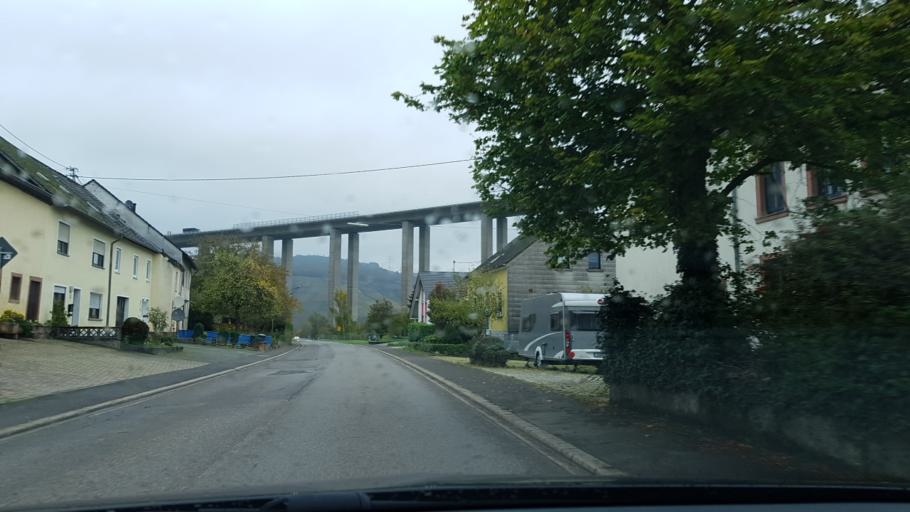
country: DE
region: Rheinland-Pfalz
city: Longuich
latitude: 49.7924
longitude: 6.7737
